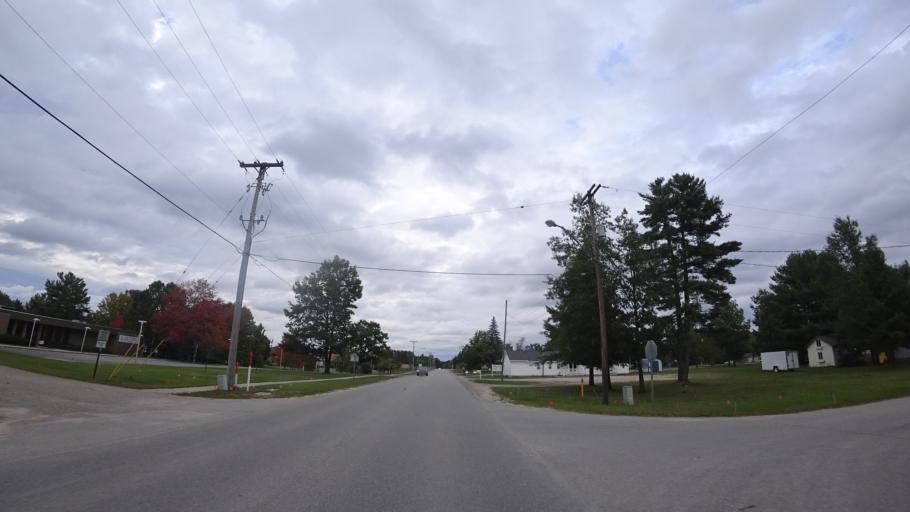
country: US
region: Michigan
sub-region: Kalkaska County
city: Kalkaska
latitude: 44.7390
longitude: -85.1845
